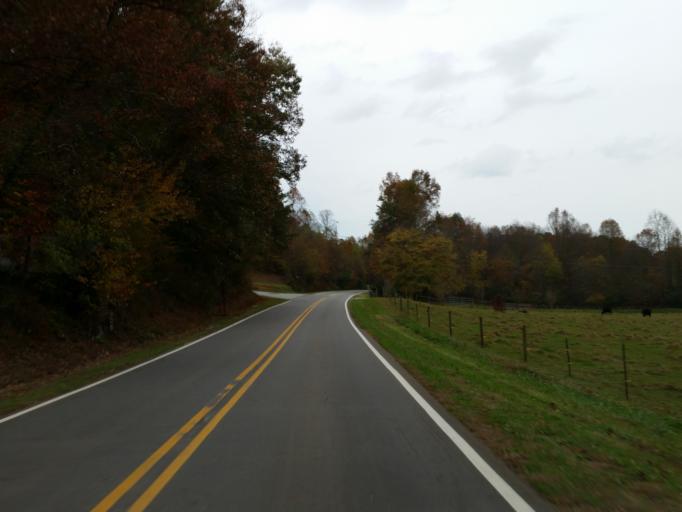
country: US
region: Georgia
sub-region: Gilmer County
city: Ellijay
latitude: 34.6609
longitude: -84.3778
